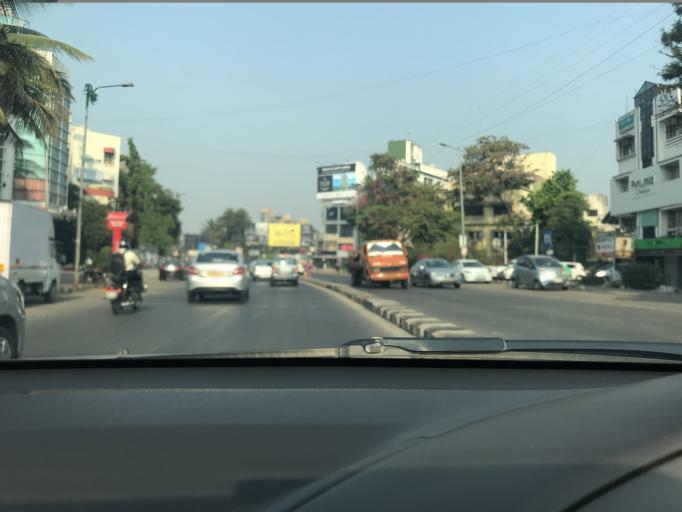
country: IN
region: Maharashtra
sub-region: Pune Division
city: Khadki
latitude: 18.5536
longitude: 73.8023
